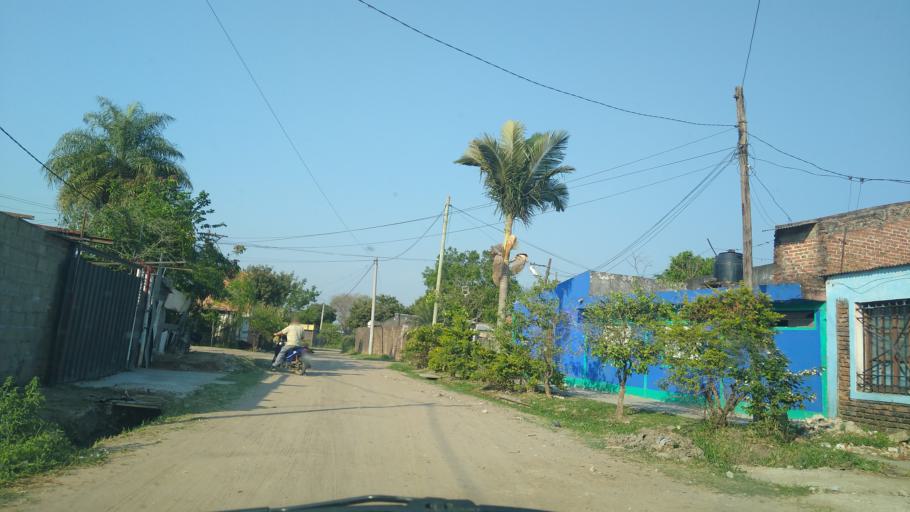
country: AR
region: Chaco
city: Barranqueras
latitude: -27.4775
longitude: -58.9285
